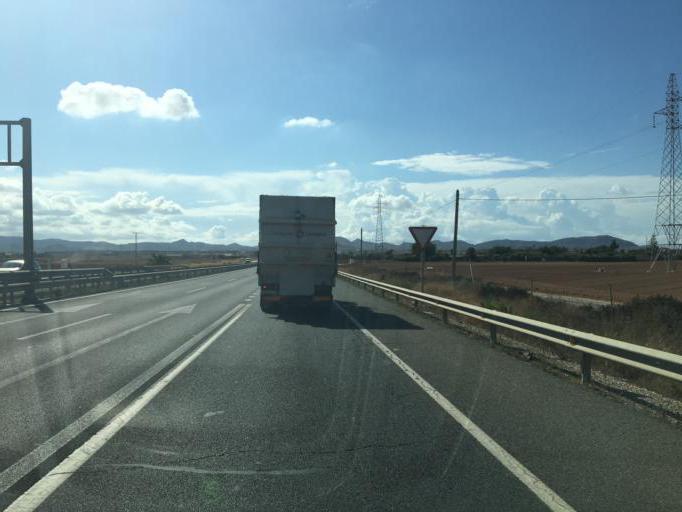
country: ES
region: Murcia
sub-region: Murcia
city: Cartagena
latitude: 37.6546
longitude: -0.9792
